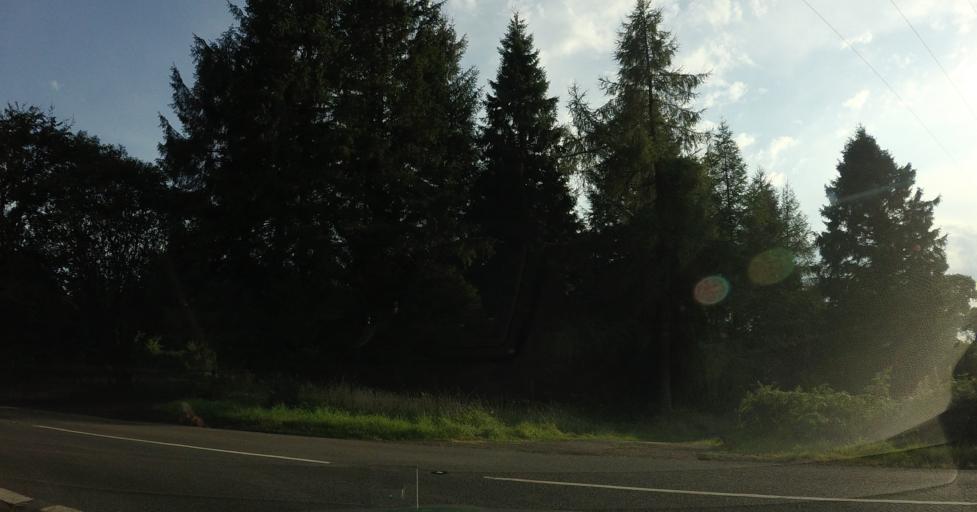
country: GB
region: Scotland
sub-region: Perth and Kinross
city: Auchterarder
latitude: 56.2959
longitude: -3.7654
